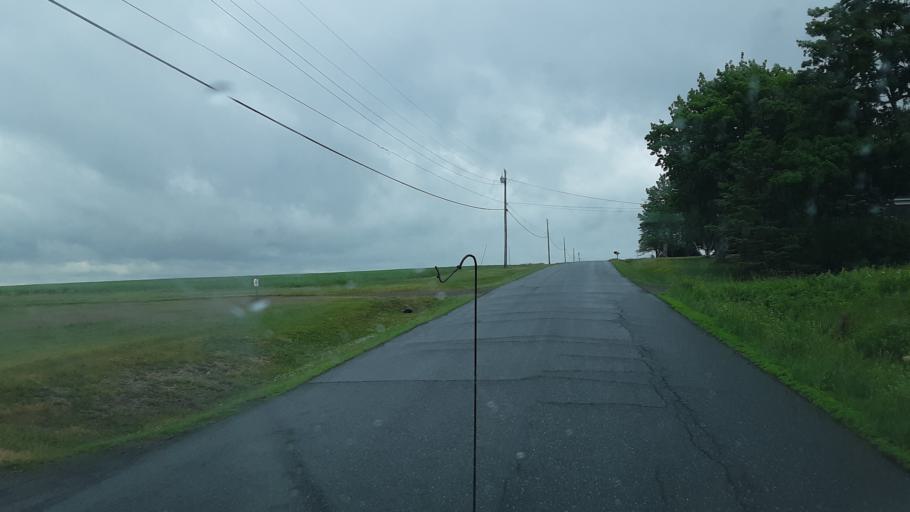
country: US
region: Maine
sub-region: Aroostook County
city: Presque Isle
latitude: 46.6818
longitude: -68.1886
